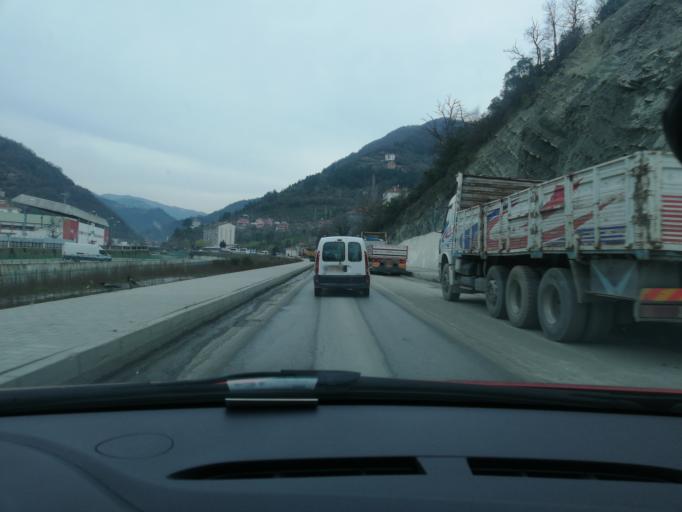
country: TR
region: Kastamonu
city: Inebolu
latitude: 41.9724
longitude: 33.7554
